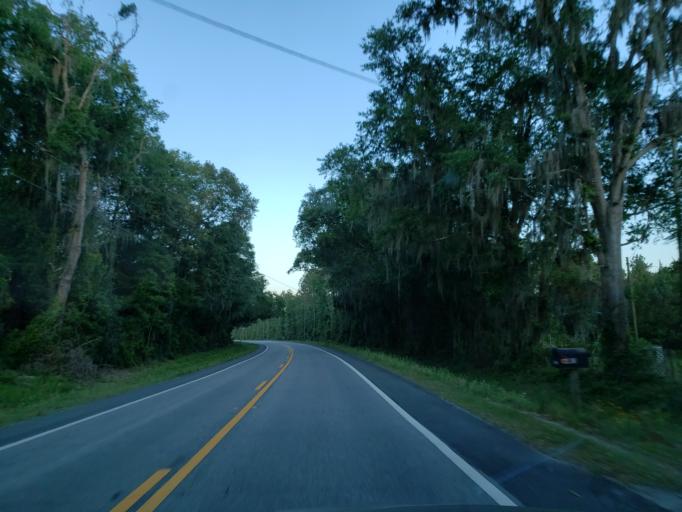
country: US
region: Georgia
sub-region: Echols County
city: Statenville
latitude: 30.5563
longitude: -83.1229
